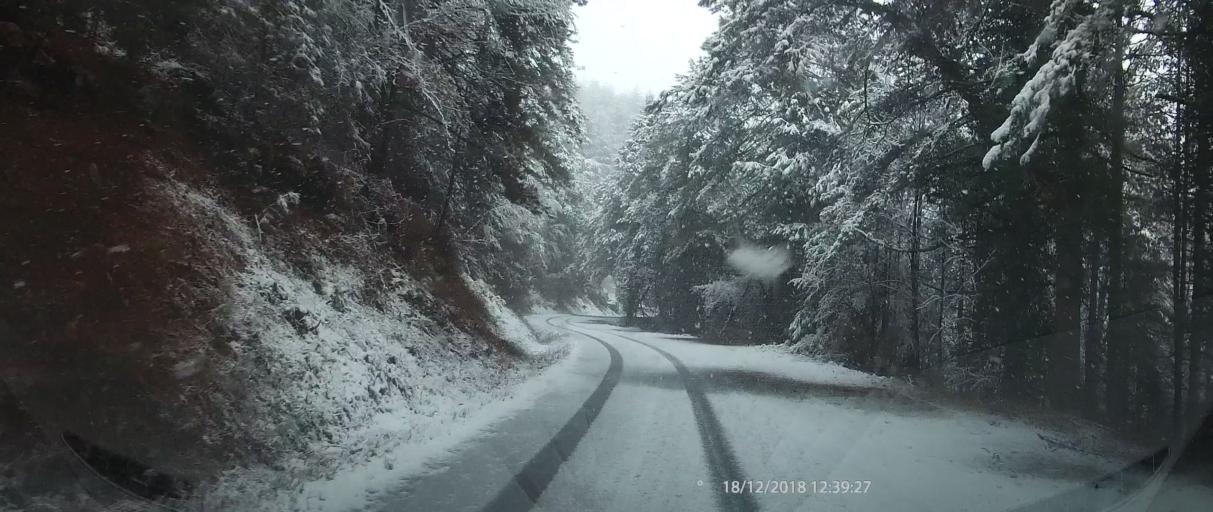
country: GR
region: Central Macedonia
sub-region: Nomos Pierias
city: Litochoro
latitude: 40.0914
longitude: 22.4161
